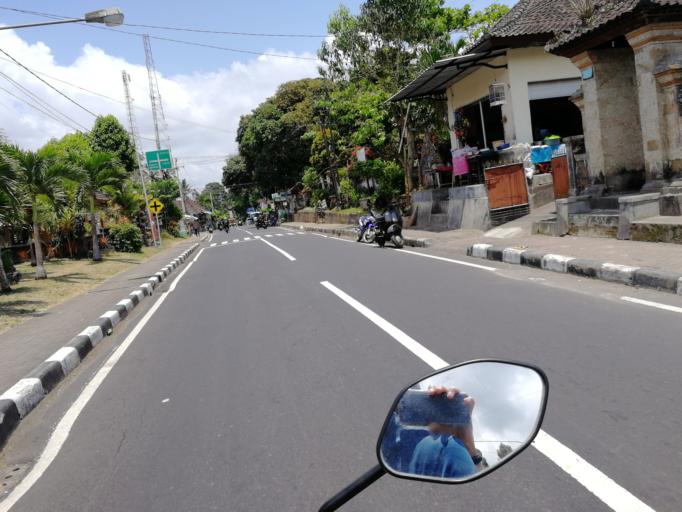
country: ID
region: Bali
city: Bangli
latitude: -8.4520
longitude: 115.3857
